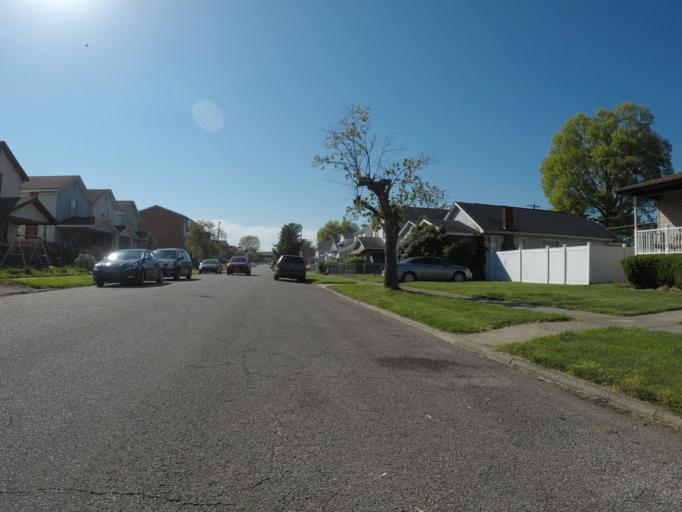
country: US
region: West Virginia
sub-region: Wayne County
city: Kenova
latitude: 38.3971
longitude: -82.5708
